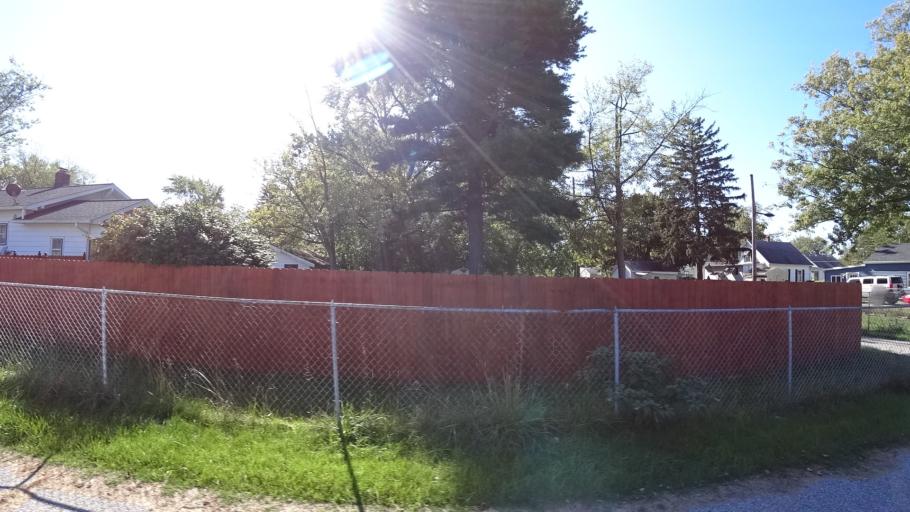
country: US
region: Indiana
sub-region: LaPorte County
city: Michigan City
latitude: 41.7098
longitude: -86.8838
